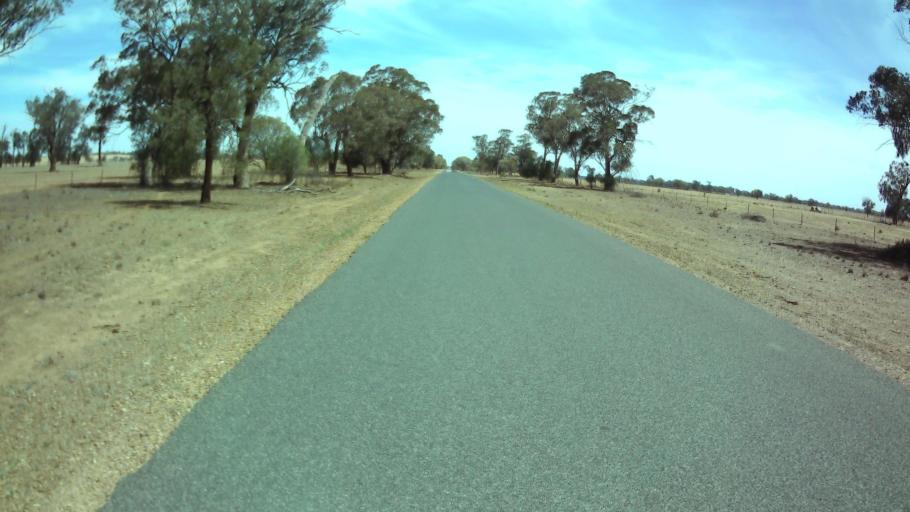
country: AU
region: New South Wales
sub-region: Weddin
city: Grenfell
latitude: -33.8667
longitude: 147.7455
